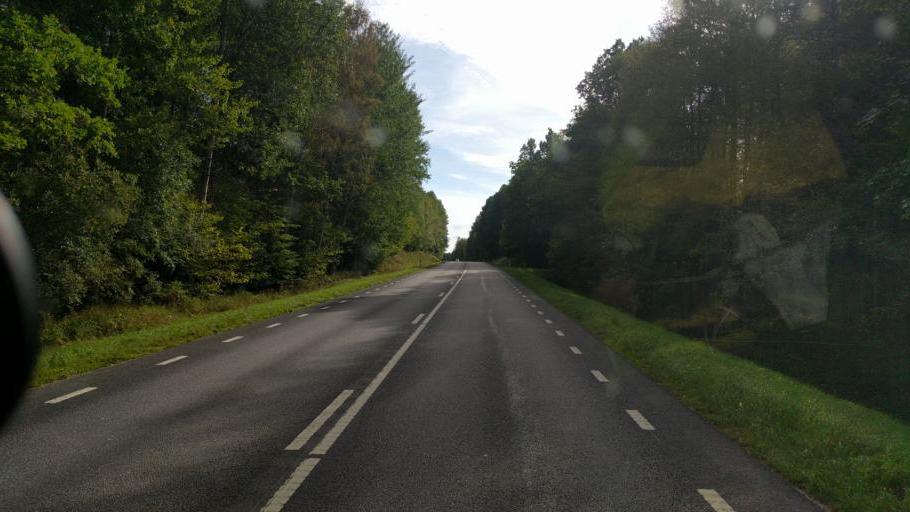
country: SE
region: OEstergoetland
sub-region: Kinda Kommun
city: Kisa
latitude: 57.9400
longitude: 15.6673
